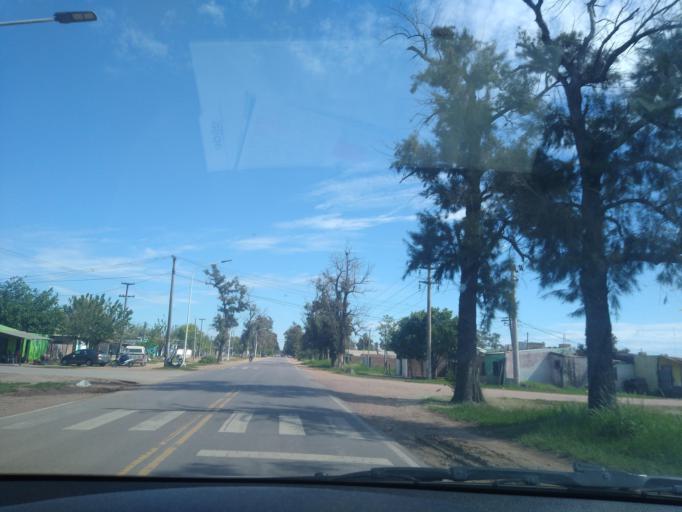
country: AR
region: Chaco
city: Presidencia Roque Saenz Pena
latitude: -26.7748
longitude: -60.4128
